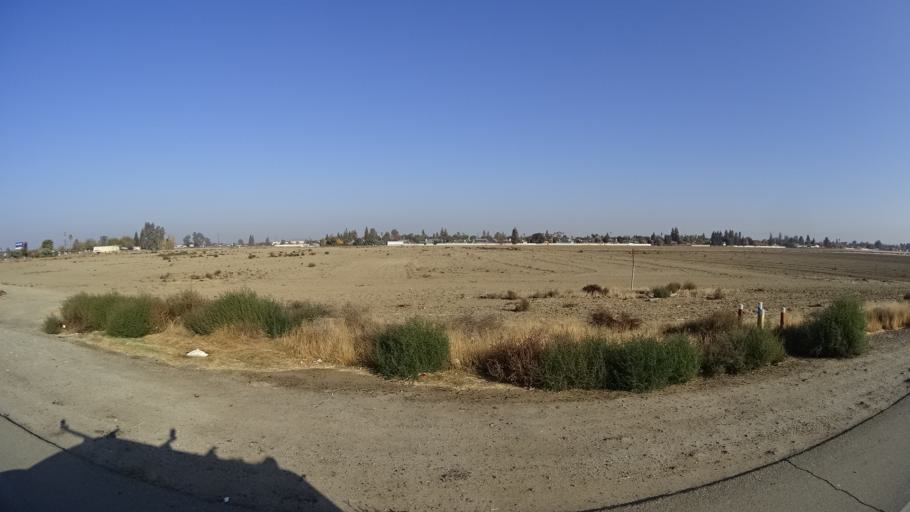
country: US
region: California
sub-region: Kern County
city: Greenfield
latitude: 35.2666
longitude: -119.0195
